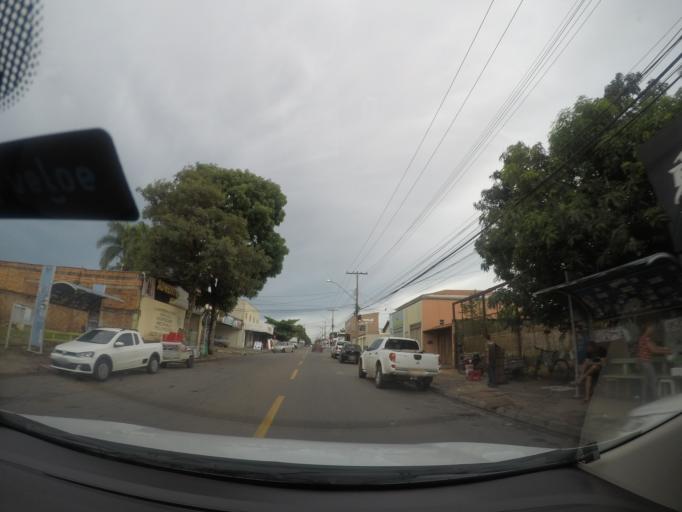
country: BR
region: Goias
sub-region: Goiania
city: Goiania
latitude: -16.7005
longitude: -49.3076
